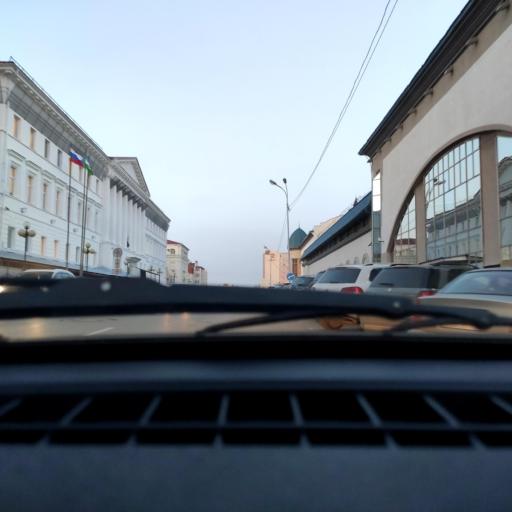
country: RU
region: Bashkortostan
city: Ufa
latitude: 54.7186
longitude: 55.9375
